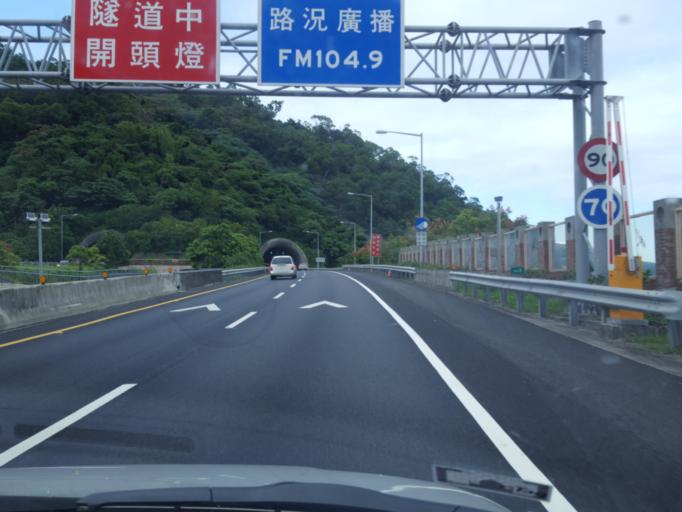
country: TW
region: Taiwan
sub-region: Yilan
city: Yilan
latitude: 24.8462
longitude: 121.7909
